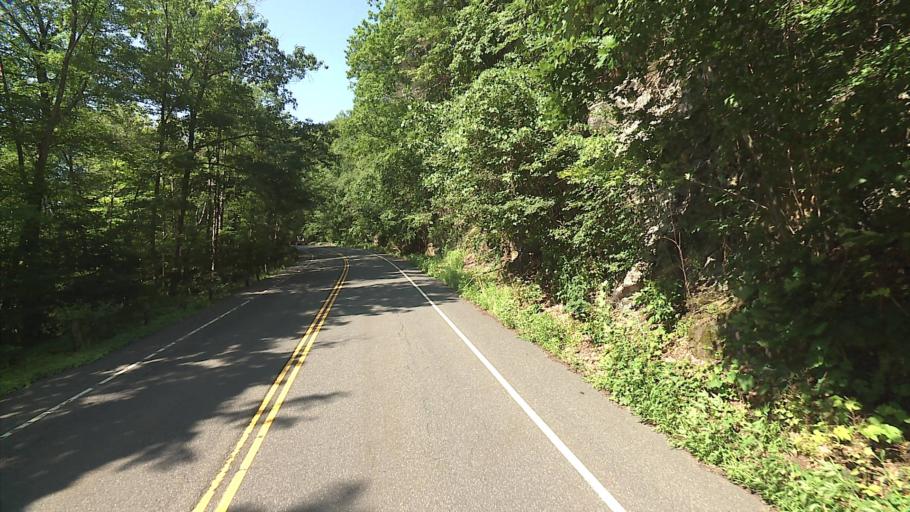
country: US
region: Massachusetts
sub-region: Hampden County
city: Granville
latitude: 42.0289
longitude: -72.9413
